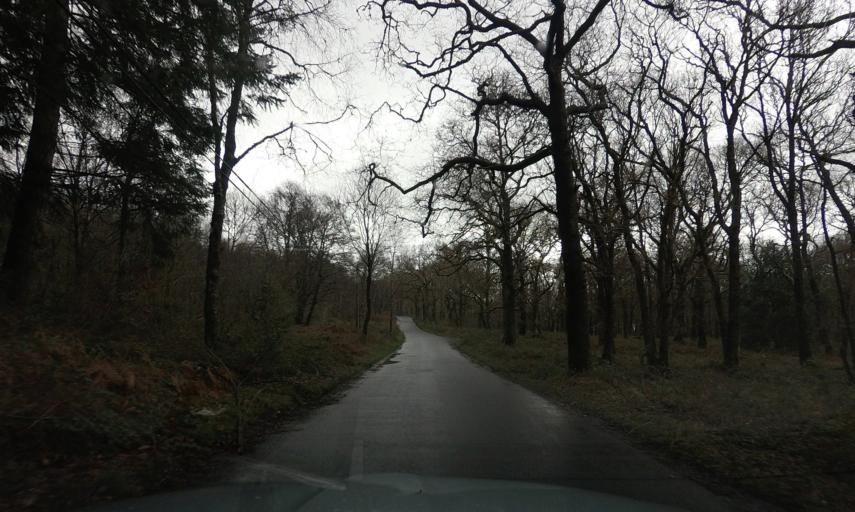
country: GB
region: Scotland
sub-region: West Dunbartonshire
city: Balloch
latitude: 56.1258
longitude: -4.6031
